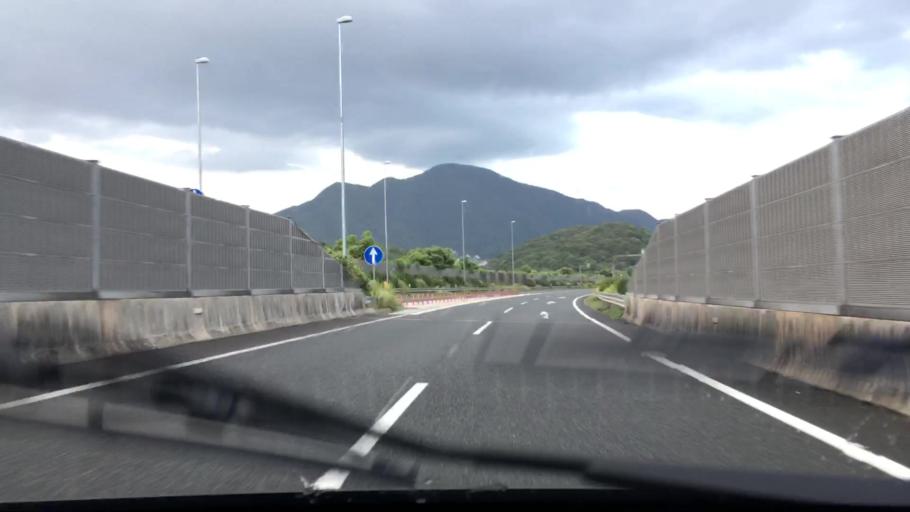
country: JP
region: Fukuoka
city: Kitakyushu
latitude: 33.8213
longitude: 130.8873
